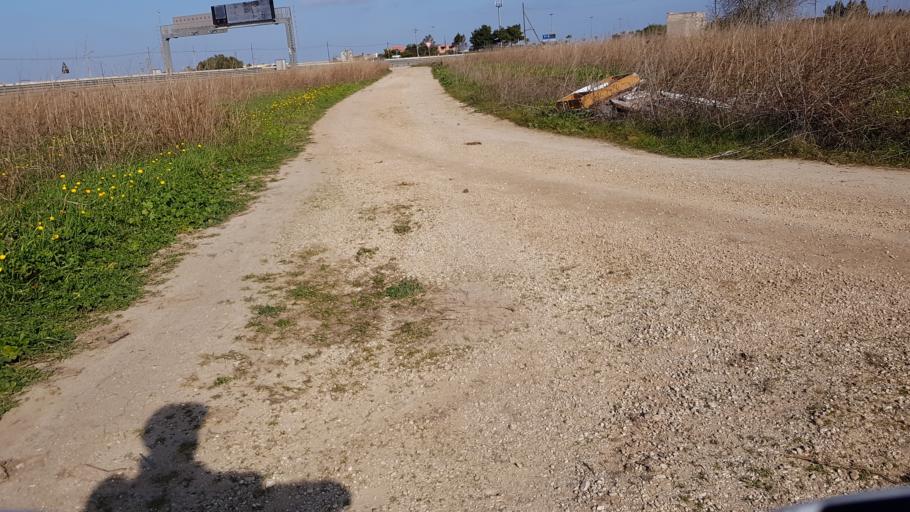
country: IT
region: Apulia
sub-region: Provincia di Brindisi
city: Brindisi
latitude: 40.6135
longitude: 17.8996
